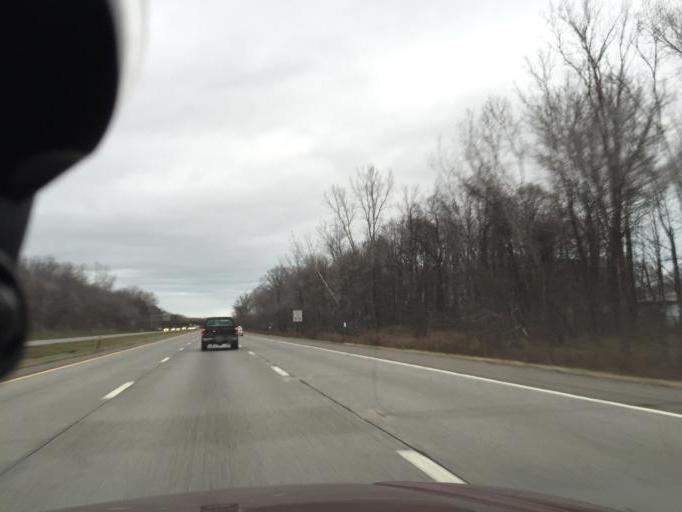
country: US
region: New York
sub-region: Monroe County
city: Greece
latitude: 43.2138
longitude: -77.6746
